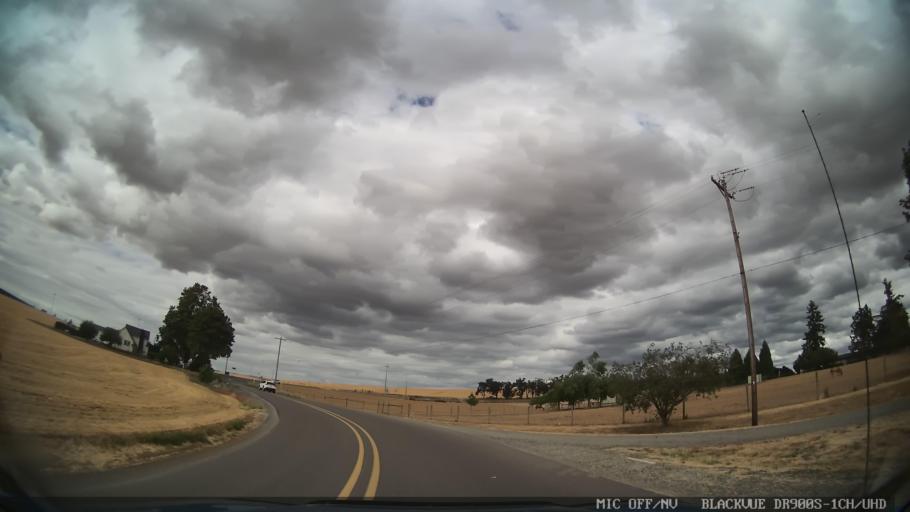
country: US
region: Oregon
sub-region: Marion County
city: Sublimity
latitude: 44.8664
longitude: -122.7558
